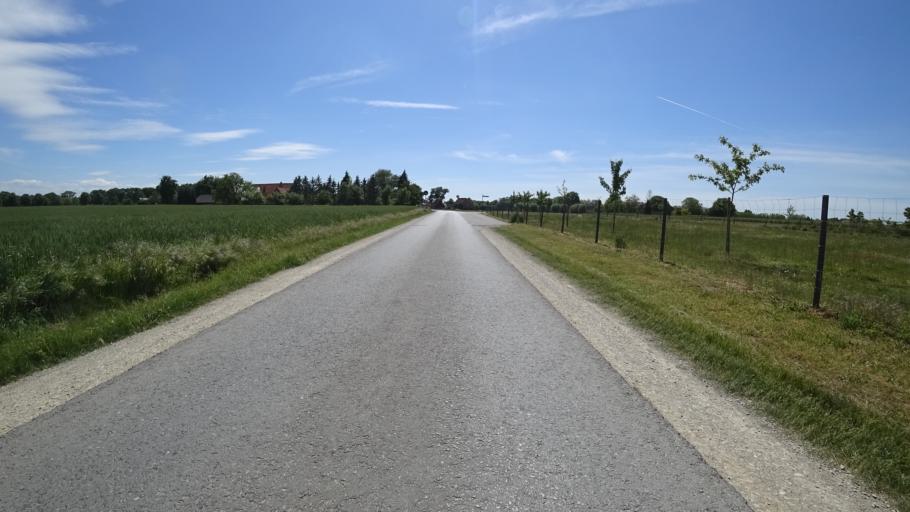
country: DE
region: North Rhine-Westphalia
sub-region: Regierungsbezirk Detmold
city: Rheda-Wiedenbruck
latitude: 51.8208
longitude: 8.3206
